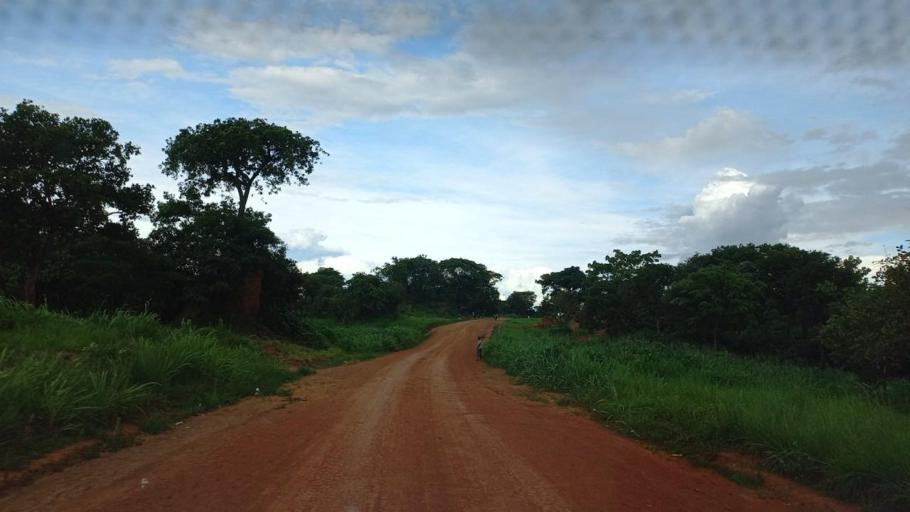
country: ZM
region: North-Western
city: Mwinilunga
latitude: -11.7588
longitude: 24.4209
